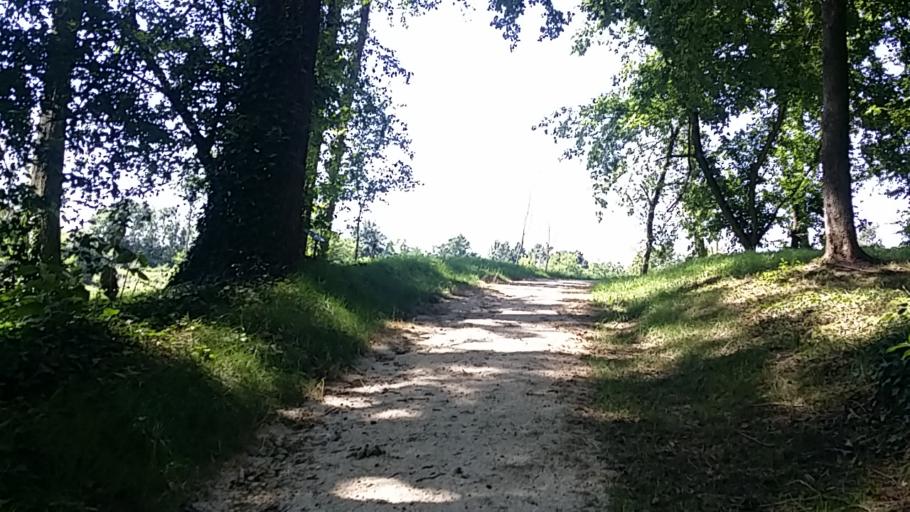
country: HU
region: Fejer
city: Deg
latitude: 46.8616
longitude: 18.4273
